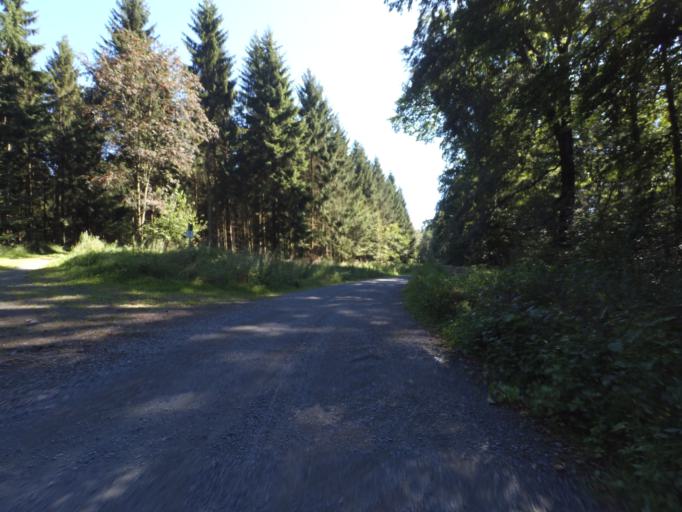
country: DE
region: Rheinland-Pfalz
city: Horscheid
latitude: 50.2074
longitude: 6.8626
